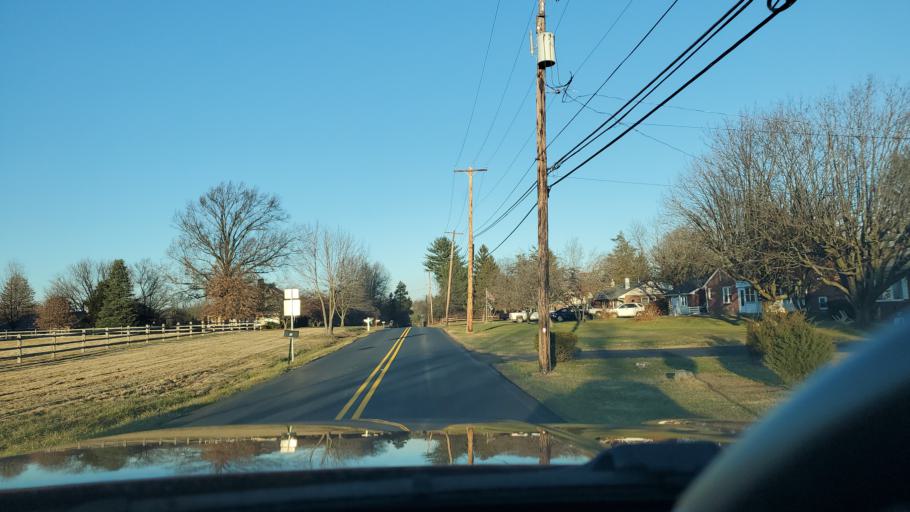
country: US
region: Pennsylvania
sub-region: Montgomery County
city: Spring Mount
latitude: 40.2963
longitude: -75.5176
